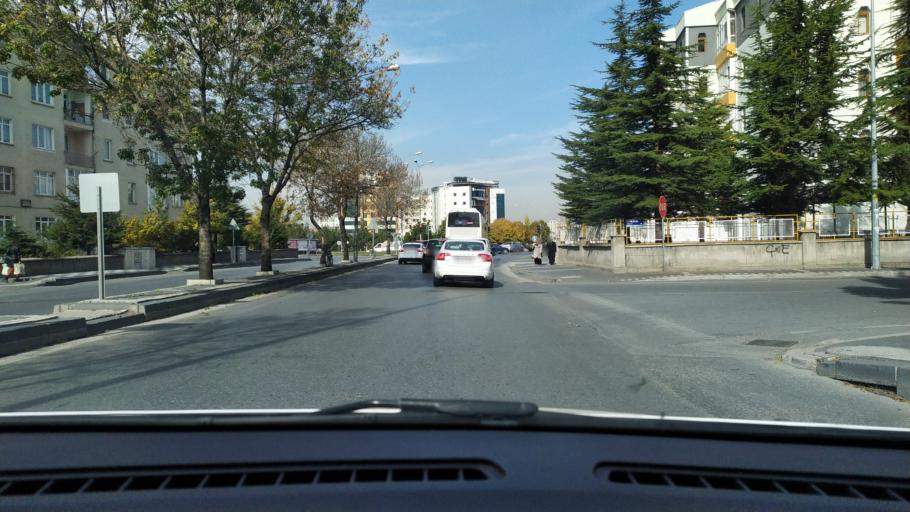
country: TR
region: Kayseri
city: Kayseri
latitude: 38.7101
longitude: 35.4913
